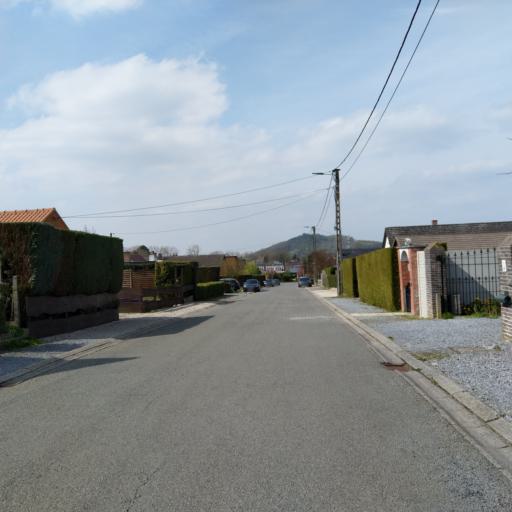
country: BE
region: Wallonia
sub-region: Province du Hainaut
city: Chasse Royale
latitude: 50.4219
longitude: 3.9582
